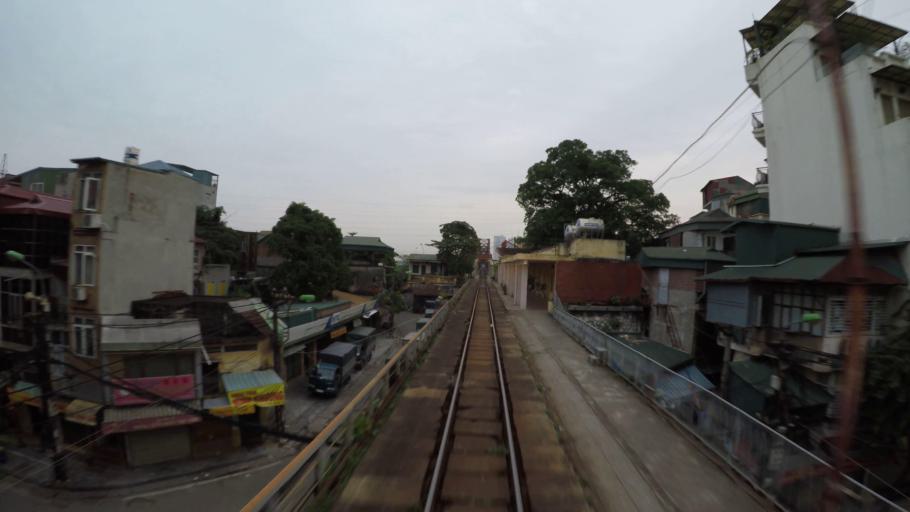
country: VN
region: Ha Noi
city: Hoan Kiem
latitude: 21.0466
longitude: 105.8669
